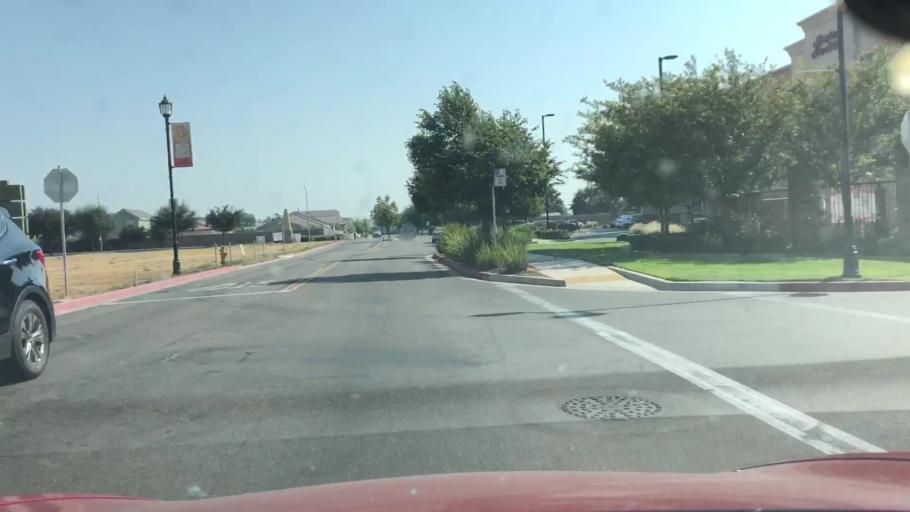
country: US
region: California
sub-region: San Joaquin County
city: Manteca
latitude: 37.7806
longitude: -121.2260
